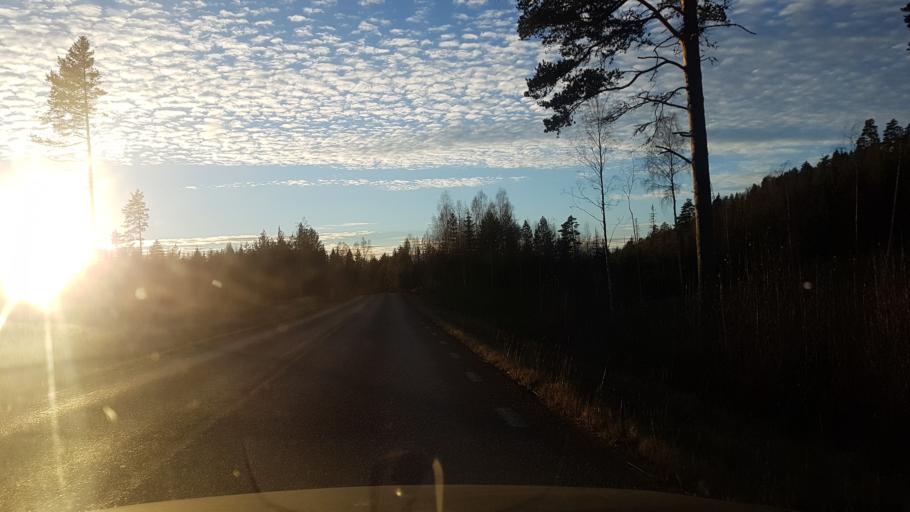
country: SE
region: Dalarna
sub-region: Leksand Municipality
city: Smedby
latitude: 60.7181
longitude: 15.1043
